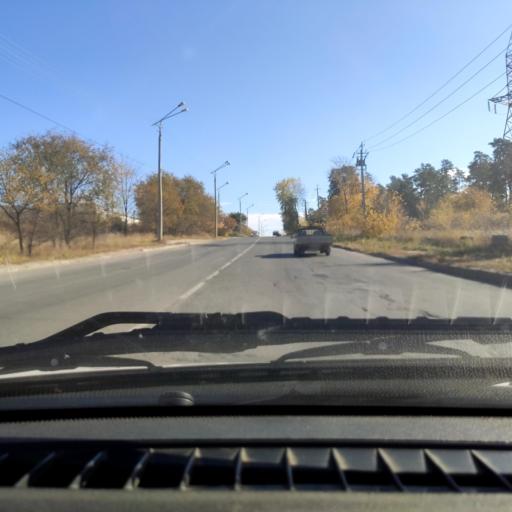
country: RU
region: Samara
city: Zhigulevsk
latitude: 53.4718
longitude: 49.5417
